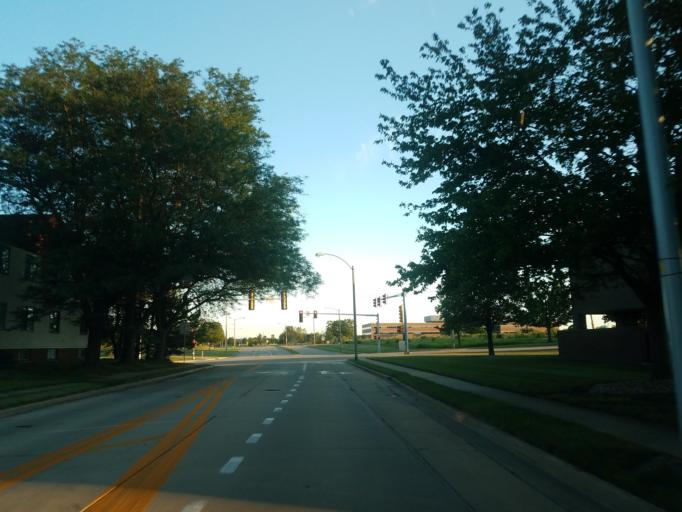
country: US
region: Illinois
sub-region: McLean County
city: Bloomington
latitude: 40.4669
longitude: -88.9501
